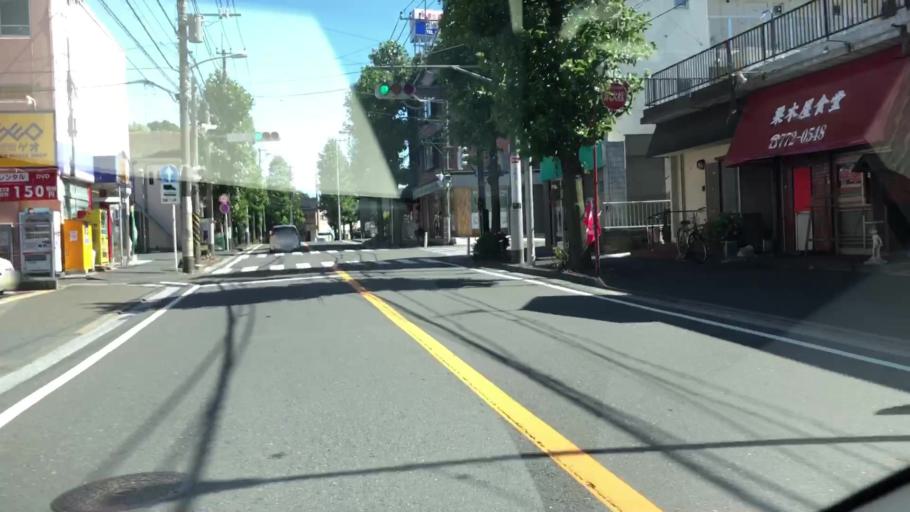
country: JP
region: Kanagawa
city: Yokohama
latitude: 35.3813
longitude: 139.6064
